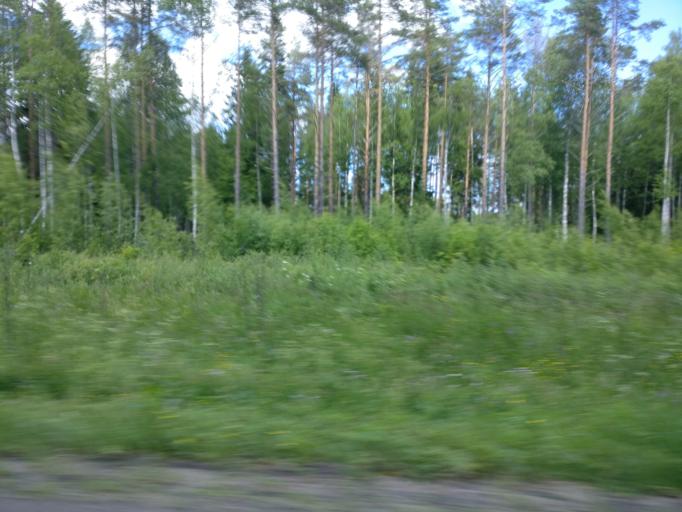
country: FI
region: Southern Savonia
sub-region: Savonlinna
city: Kerimaeki
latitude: 61.8506
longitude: 29.1746
